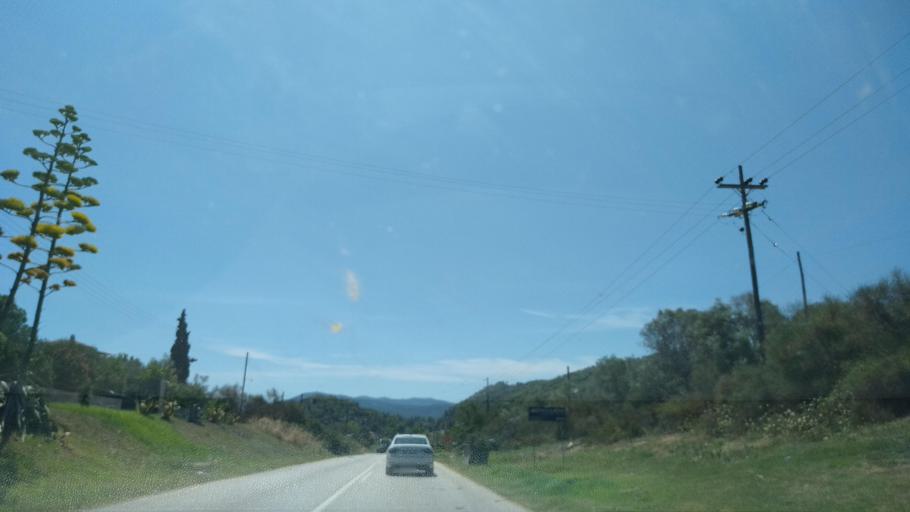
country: GR
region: Central Macedonia
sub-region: Nomos Chalkidikis
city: Agios Nikolaos
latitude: 40.2255
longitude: 23.7433
